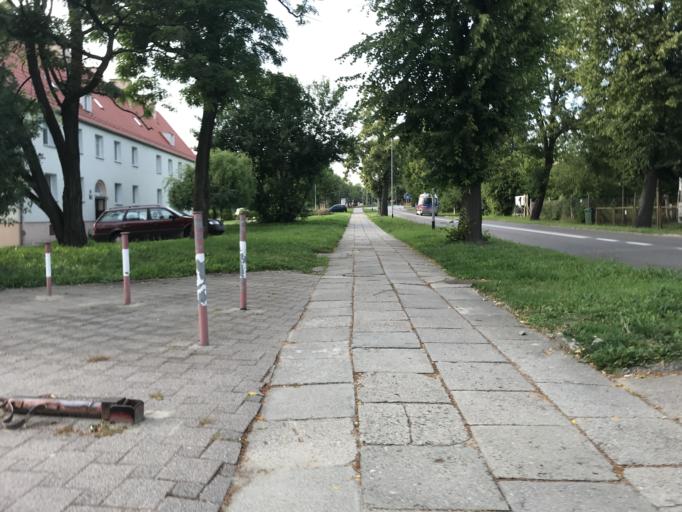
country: PL
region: Warmian-Masurian Voivodeship
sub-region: Powiat elblaski
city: Elblag
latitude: 54.1659
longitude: 19.4246
